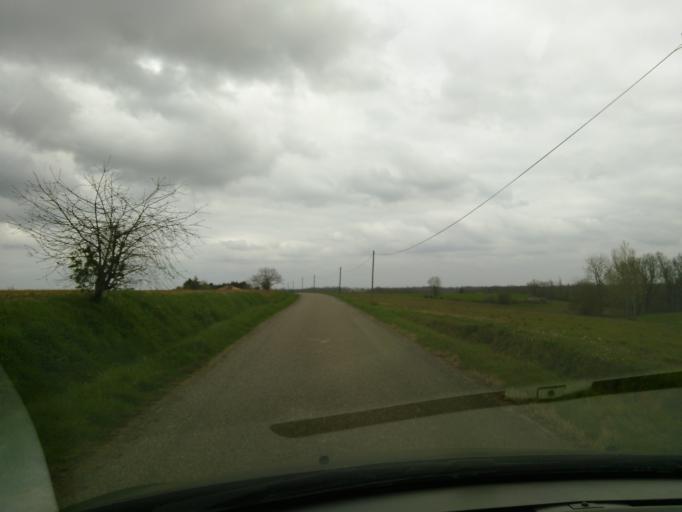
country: FR
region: Midi-Pyrenees
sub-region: Departement du Tarn-et-Garonne
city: Saint-Porquier
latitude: 43.9504
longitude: 1.1266
